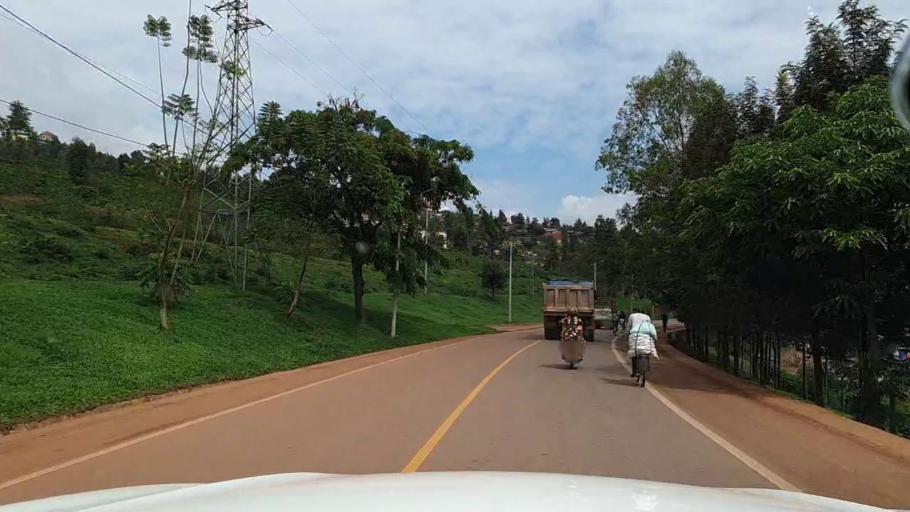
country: RW
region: Kigali
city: Kigali
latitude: -1.9123
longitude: 30.0478
